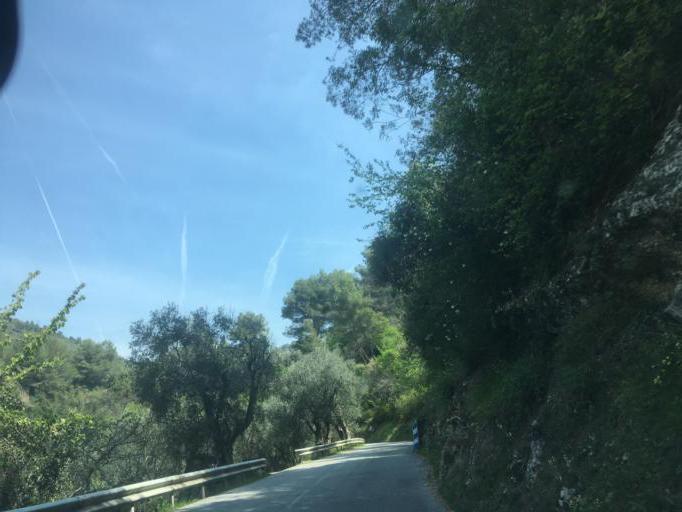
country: FR
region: Provence-Alpes-Cote d'Azur
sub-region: Departement des Alpes-Maritimes
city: Saint-Martin-du-Var
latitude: 43.8293
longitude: 7.1957
